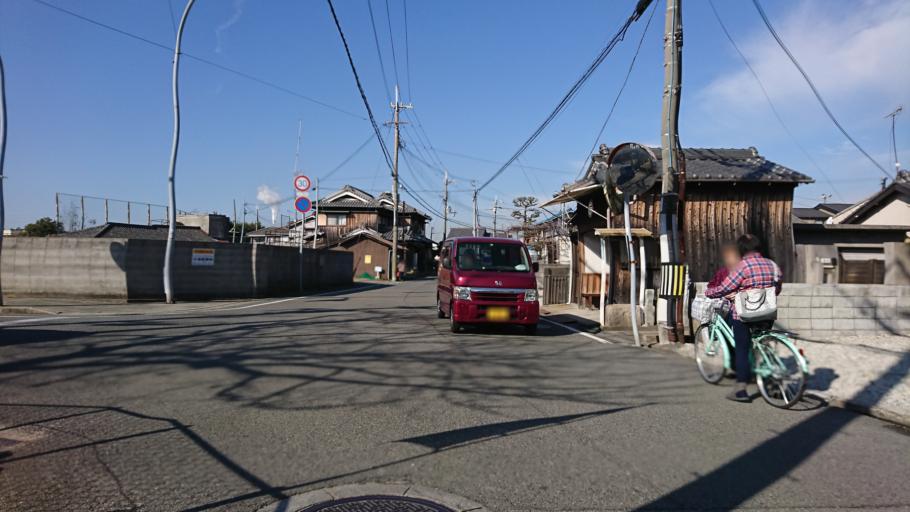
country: JP
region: Hyogo
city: Kakogawacho-honmachi
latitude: 34.7499
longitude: 134.7985
